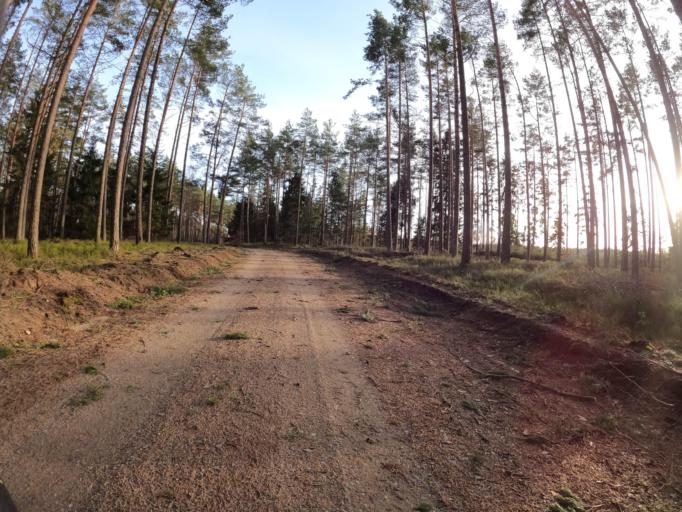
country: PL
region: West Pomeranian Voivodeship
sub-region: Powiat koszalinski
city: Polanow
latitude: 54.1543
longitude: 16.6712
